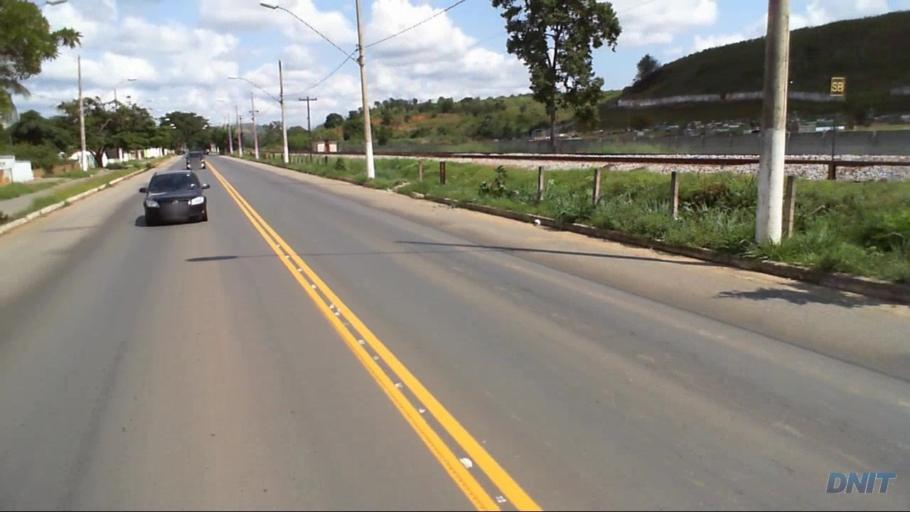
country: BR
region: Minas Gerais
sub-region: Governador Valadares
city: Governador Valadares
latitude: -18.9093
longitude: -41.9941
